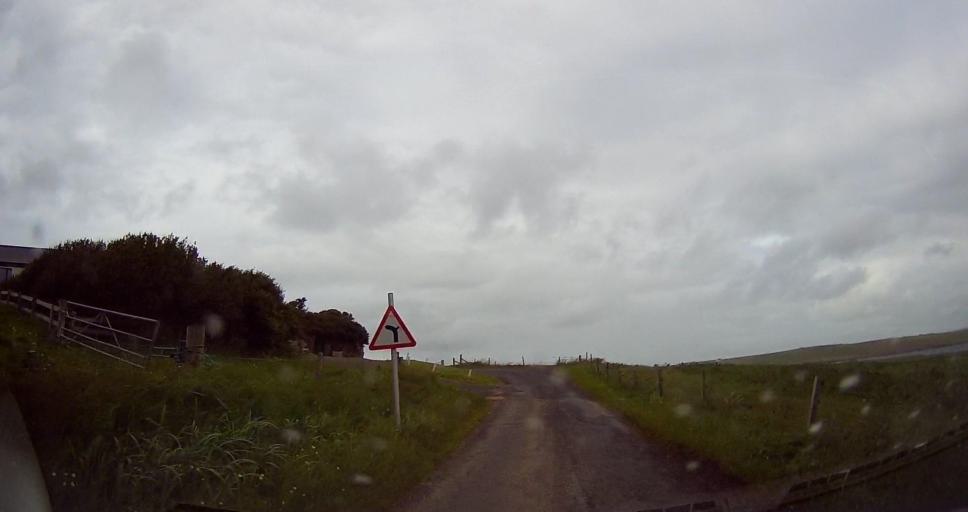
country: GB
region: Scotland
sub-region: Orkney Islands
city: Stromness
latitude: 58.9111
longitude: -3.3208
